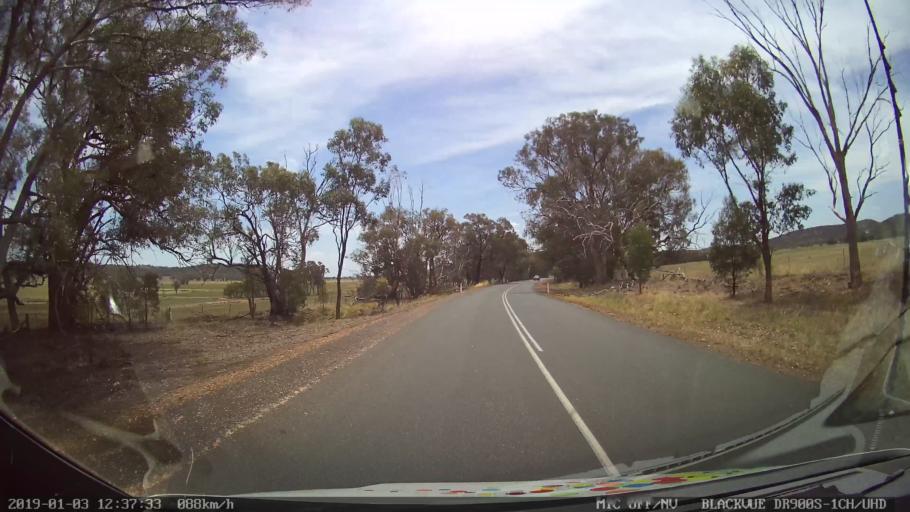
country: AU
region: New South Wales
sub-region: Weddin
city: Grenfell
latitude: -33.8414
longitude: 148.1854
